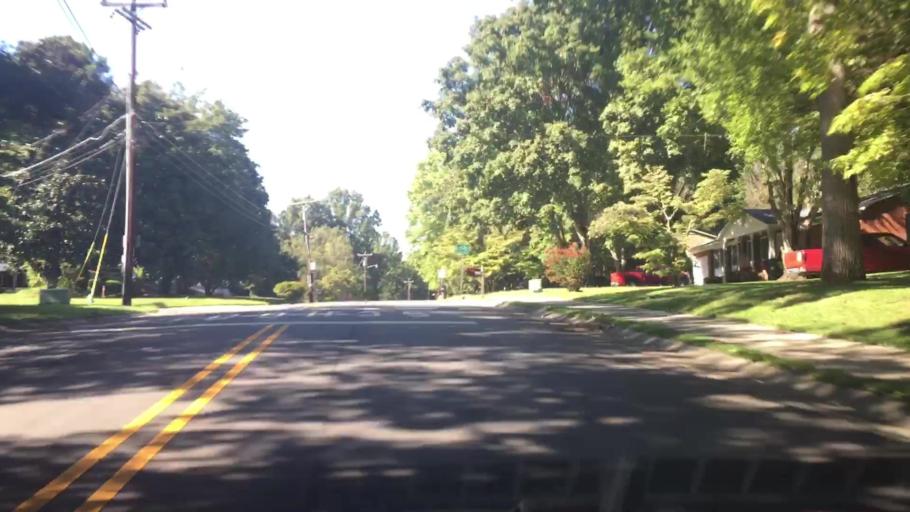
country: US
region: North Carolina
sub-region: Iredell County
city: Mooresville
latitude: 35.5653
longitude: -80.8029
